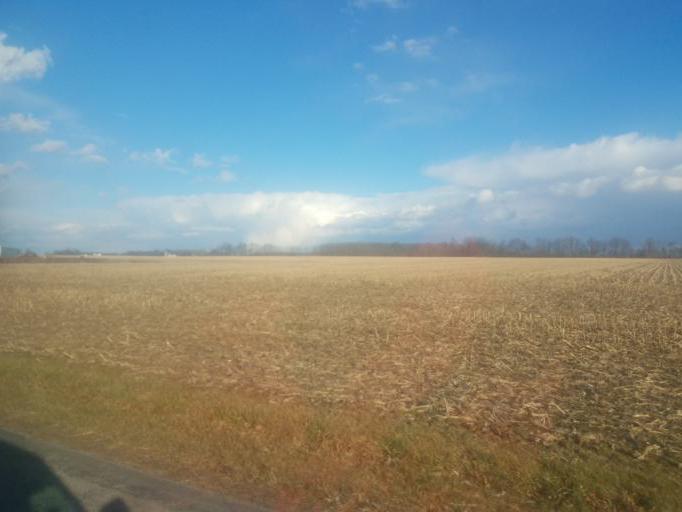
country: US
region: Ohio
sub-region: Marion County
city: Prospect
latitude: 40.4073
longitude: -83.1439
